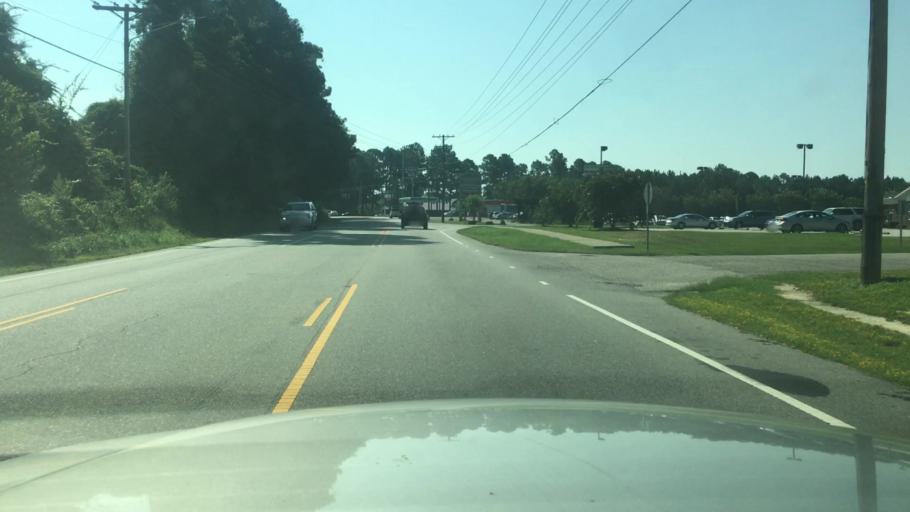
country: US
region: North Carolina
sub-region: Cumberland County
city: Fayetteville
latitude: 35.1312
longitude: -78.8996
